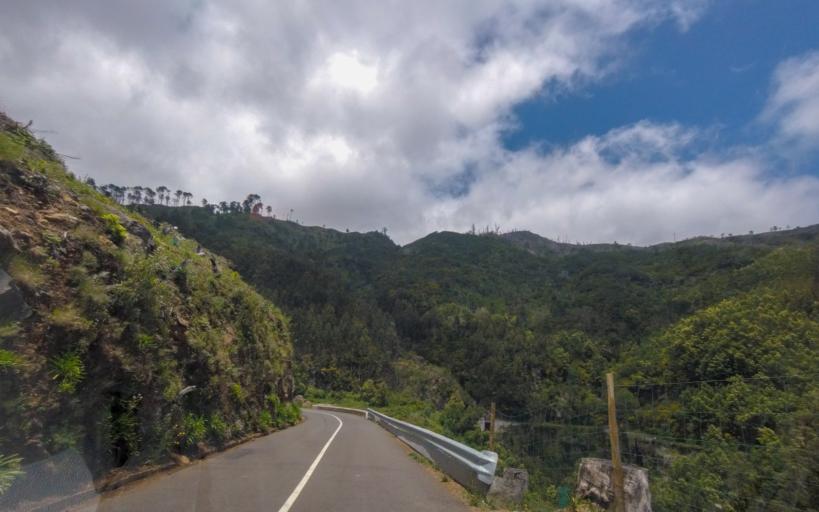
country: PT
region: Madeira
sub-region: Funchal
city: Nossa Senhora do Monte
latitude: 32.6915
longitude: -16.8969
